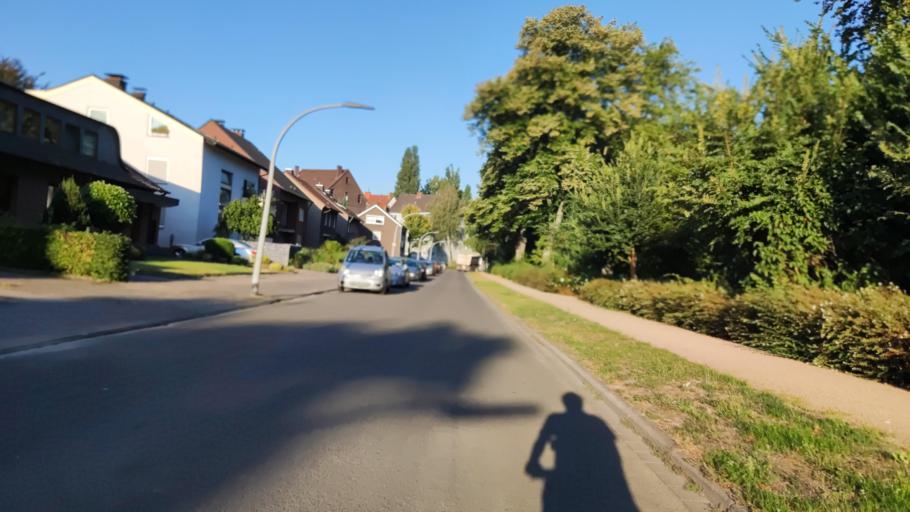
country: DE
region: North Rhine-Westphalia
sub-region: Regierungsbezirk Arnsberg
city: Herne
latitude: 51.5422
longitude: 7.2394
